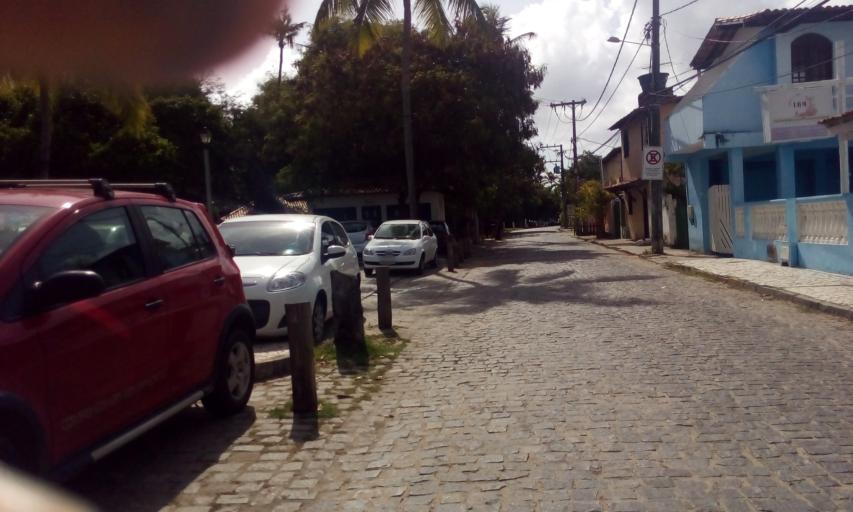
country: BR
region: Bahia
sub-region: Mata De Sao Joao
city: Mata de Sao Joao
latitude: -12.5785
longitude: -38.0063
